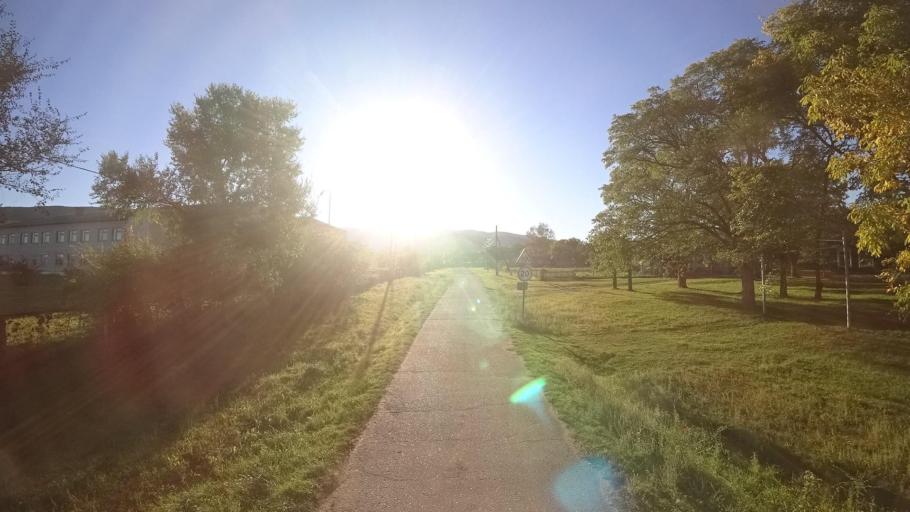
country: RU
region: Primorskiy
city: Kirovskiy
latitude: 44.8271
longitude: 133.5745
